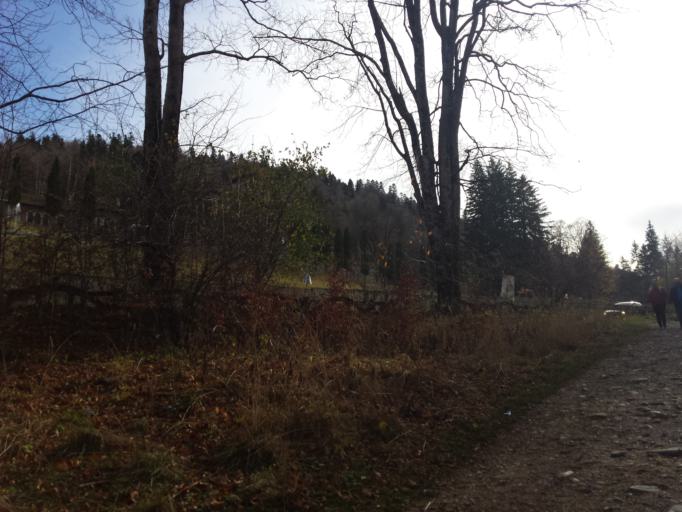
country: RO
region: Prahova
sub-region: Oras Busteni
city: Busteni
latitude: 45.4147
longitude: 25.5414
